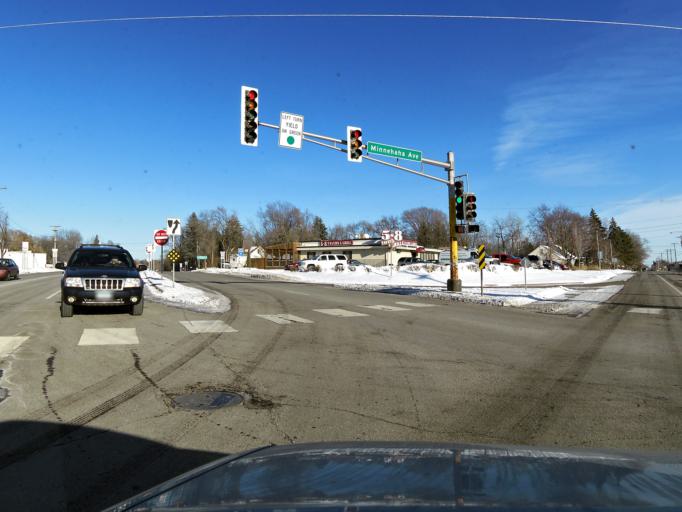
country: US
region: Minnesota
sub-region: Ramsey County
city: Maplewood
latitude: 44.9630
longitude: -93.0045
